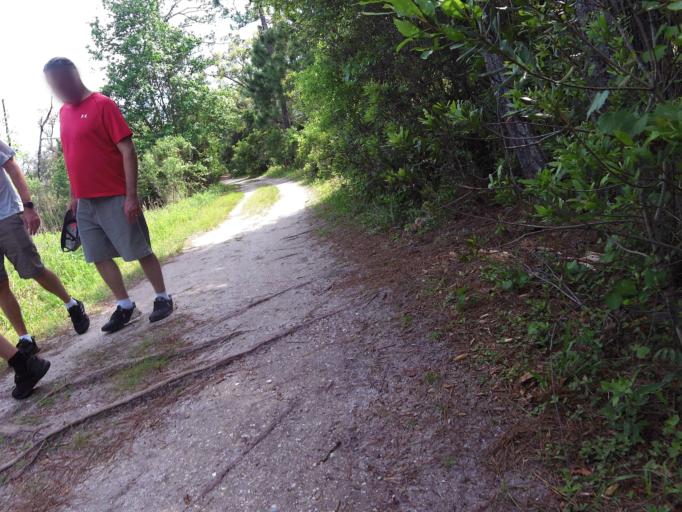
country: US
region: Florida
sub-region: Saint Johns County
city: Villano Beach
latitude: 30.0190
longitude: -81.3366
